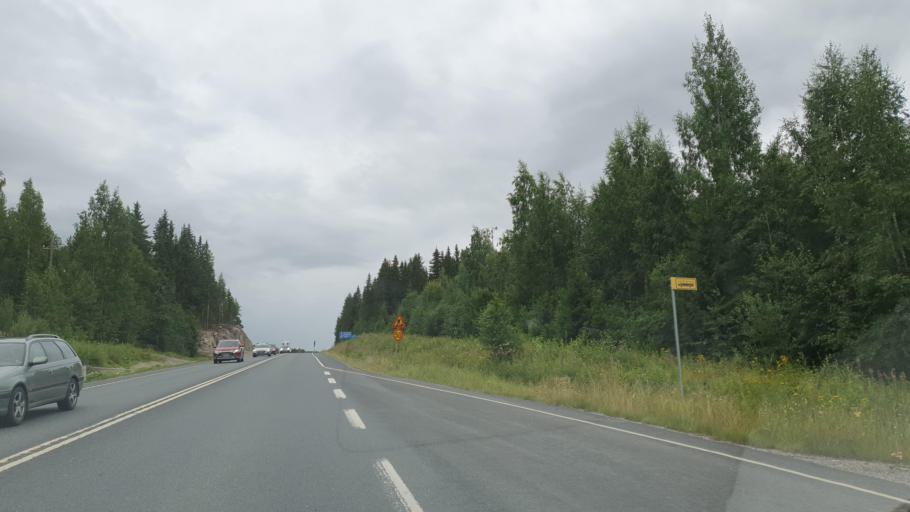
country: FI
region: Northern Savo
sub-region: Ylae-Savo
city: Lapinlahti
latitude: 63.3071
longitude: 27.4496
